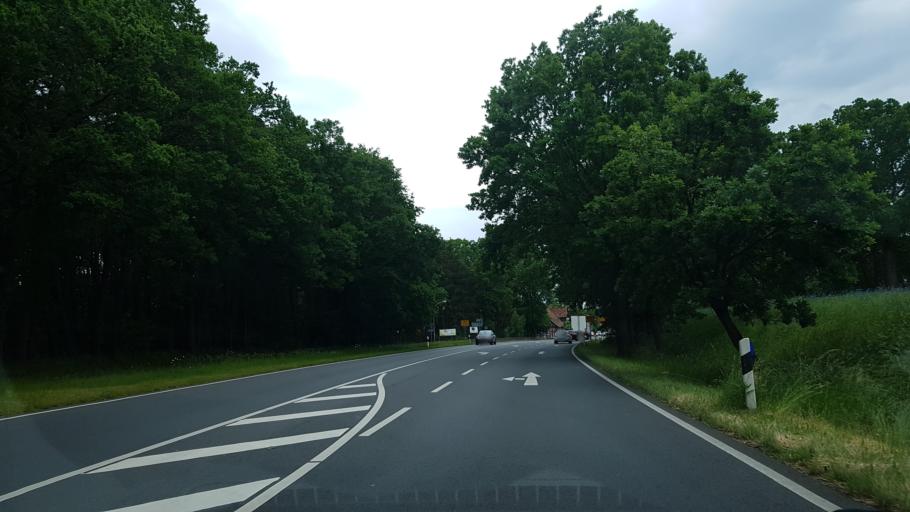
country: DE
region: Lower Saxony
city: Bergen
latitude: 52.7738
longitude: 9.9790
